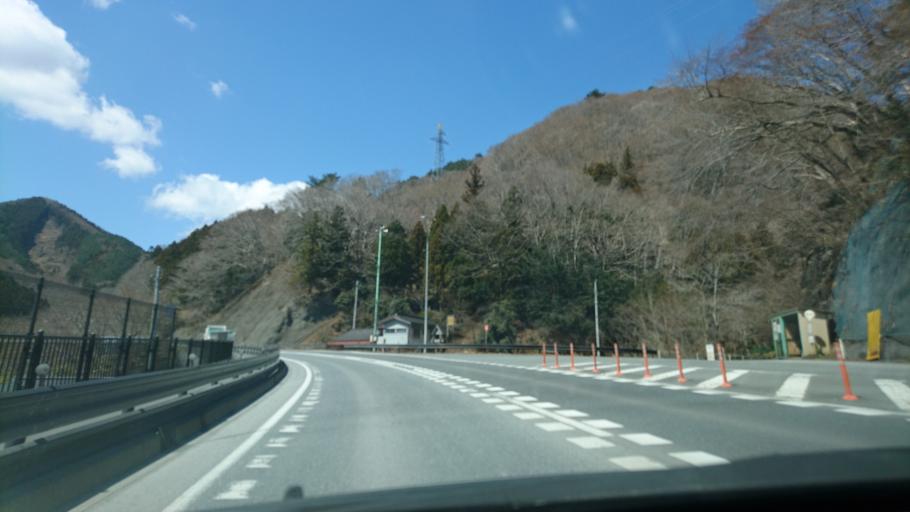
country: JP
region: Iwate
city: Ofunato
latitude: 39.1479
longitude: 141.6458
